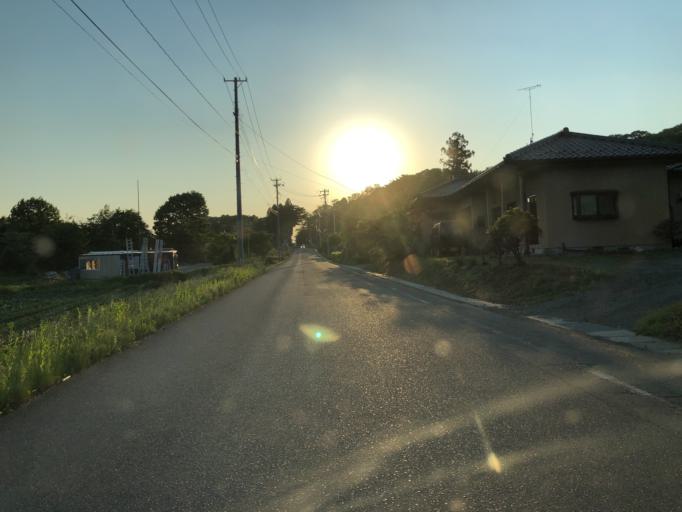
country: JP
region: Fukushima
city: Sukagawa
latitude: 37.1850
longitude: 140.3122
